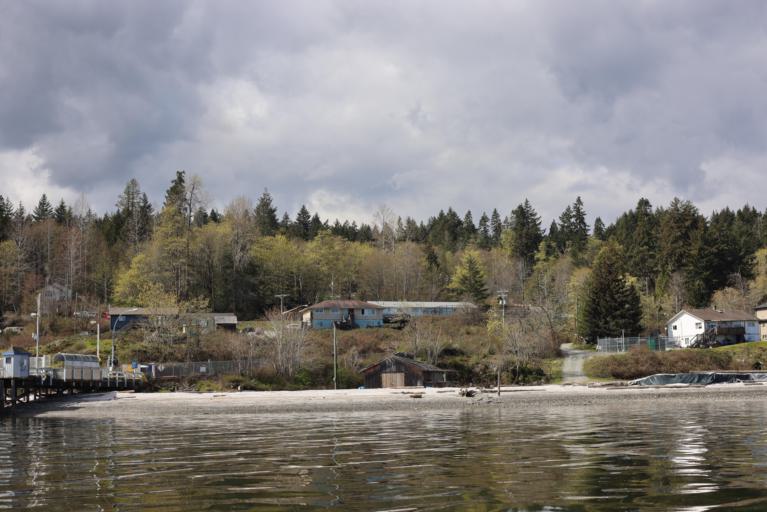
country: CA
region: British Columbia
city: North Saanich
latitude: 48.6145
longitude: -123.5168
